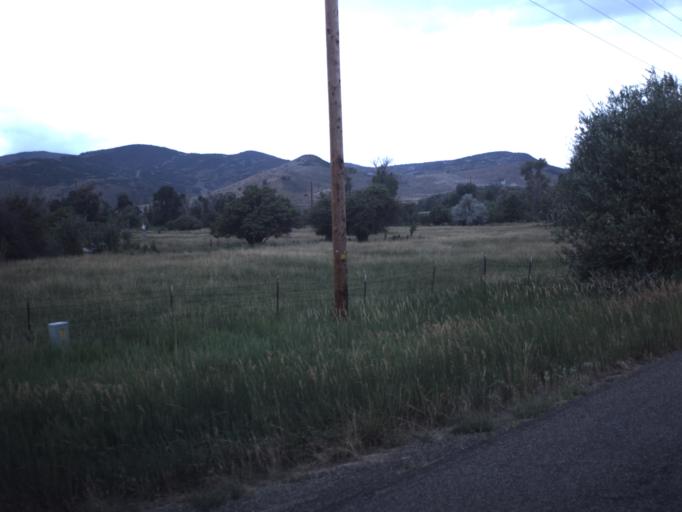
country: US
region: Utah
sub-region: Summit County
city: Coalville
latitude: 40.8131
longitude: -111.3980
